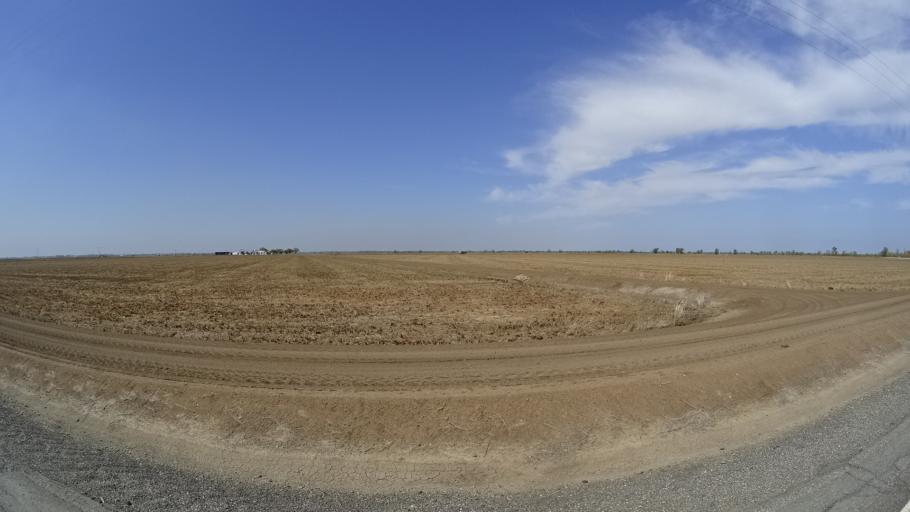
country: US
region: California
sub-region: Butte County
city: Durham
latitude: 39.5393
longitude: -121.9084
